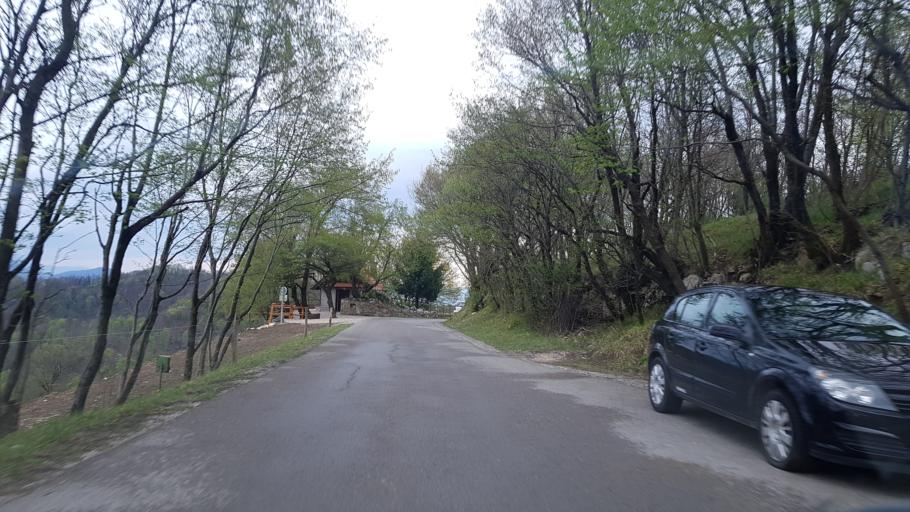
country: SI
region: Kanal
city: Deskle
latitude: 46.0388
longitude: 13.5668
